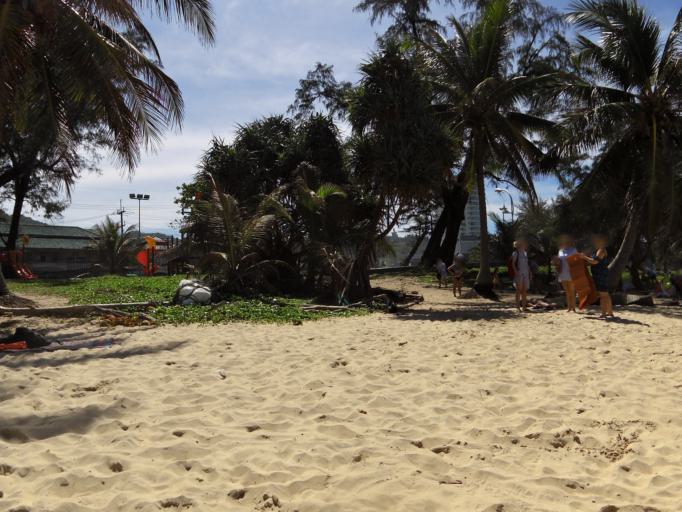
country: TH
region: Phuket
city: Ban Karon
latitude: 7.8495
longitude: 98.2924
